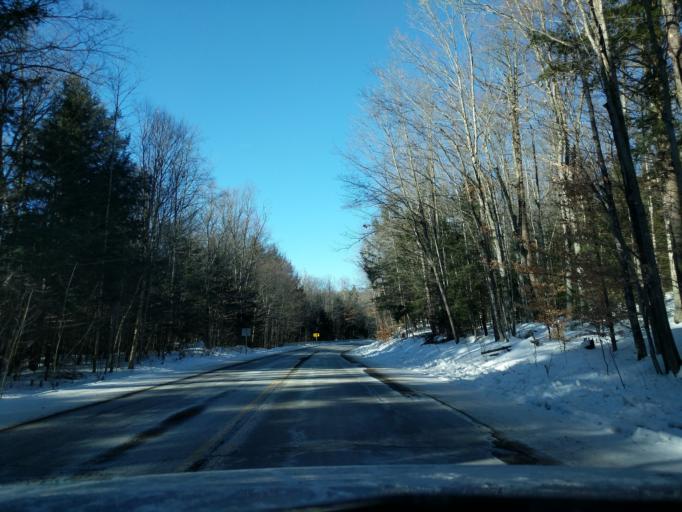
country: US
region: Wisconsin
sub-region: Menominee County
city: Keshena
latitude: 45.0925
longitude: -88.6323
